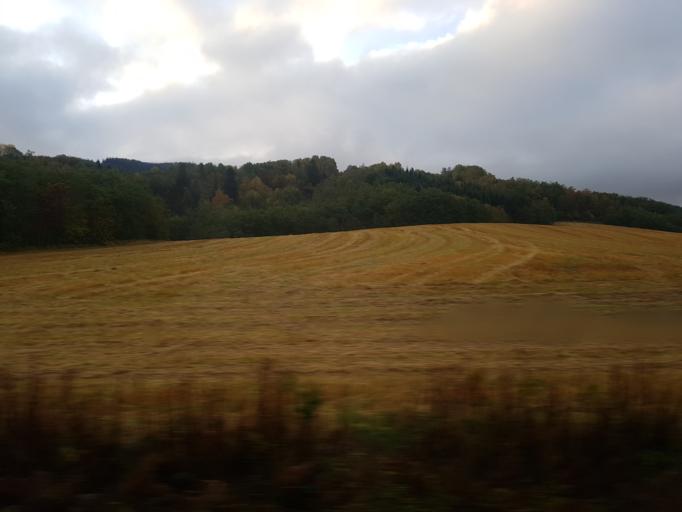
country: NO
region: Sor-Trondelag
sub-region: Melhus
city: Melhus
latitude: 63.3093
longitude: 10.2930
